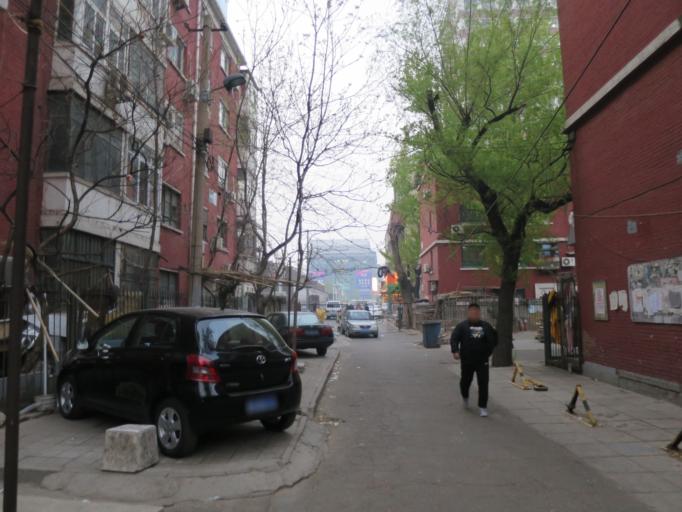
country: CN
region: Beijing
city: Chaowai
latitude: 39.9057
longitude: 116.4435
